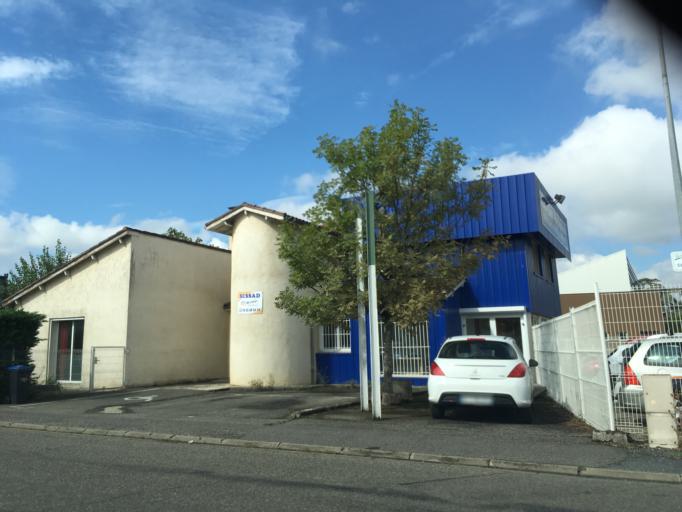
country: FR
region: Aquitaine
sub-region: Departement du Lot-et-Garonne
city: Agen
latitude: 44.1811
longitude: 0.6303
